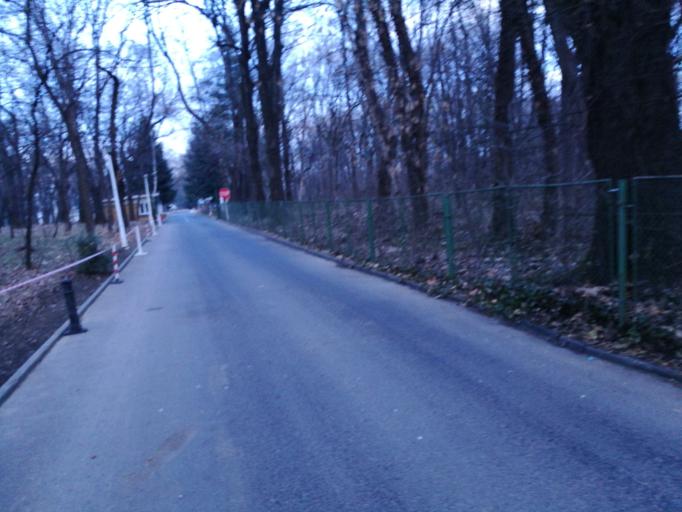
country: RO
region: Bucuresti
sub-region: Municipiul Bucuresti
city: Bucuresti
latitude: 44.4834
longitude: 26.0764
